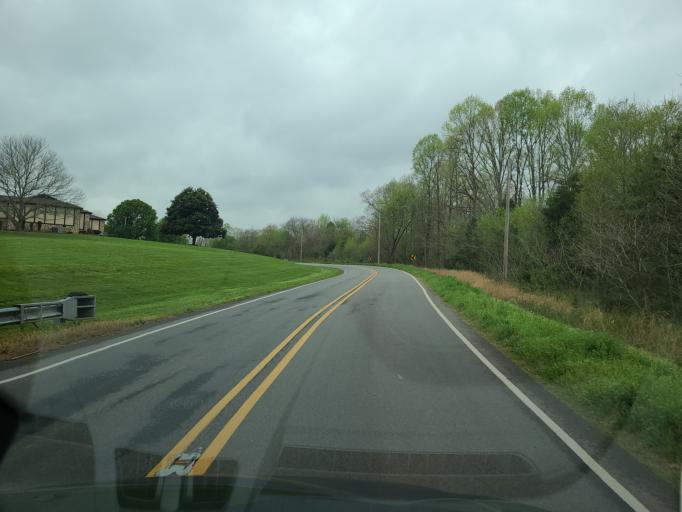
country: US
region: North Carolina
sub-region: Lincoln County
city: Lincolnton
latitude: 35.4571
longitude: -81.3372
